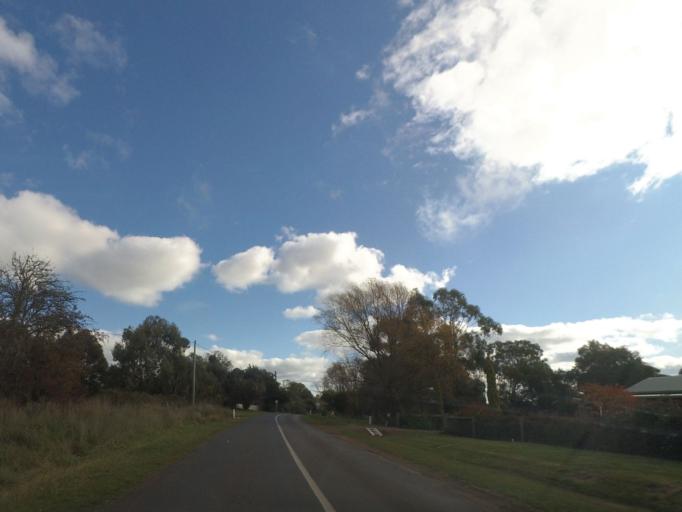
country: AU
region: Victoria
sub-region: Mount Alexander
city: Castlemaine
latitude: -37.2557
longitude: 144.4412
